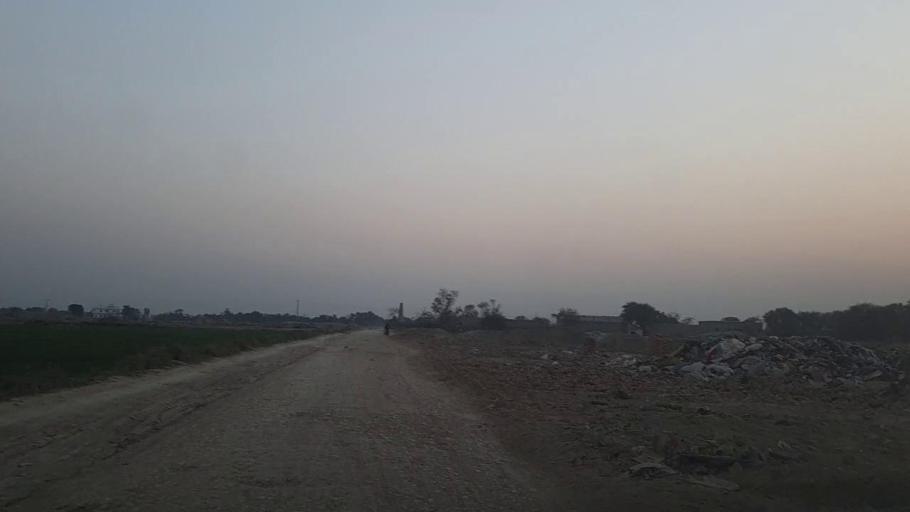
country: PK
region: Sindh
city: Naushahro Firoz
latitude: 26.8541
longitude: 68.0491
